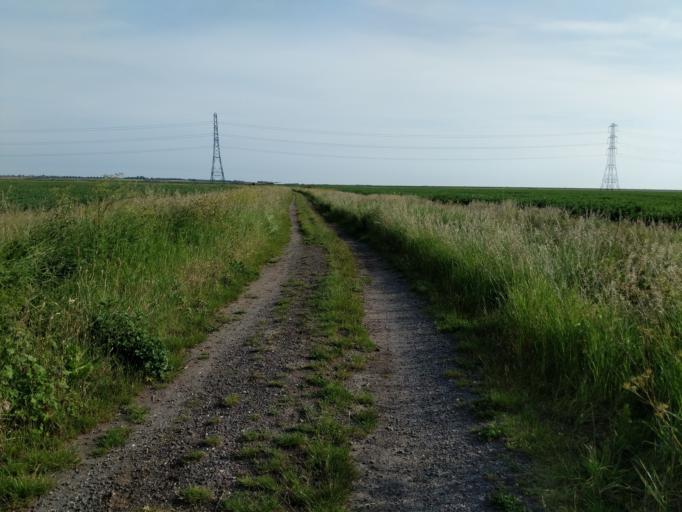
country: GB
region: England
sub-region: Kent
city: Faversham
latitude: 51.3346
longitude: 0.9151
